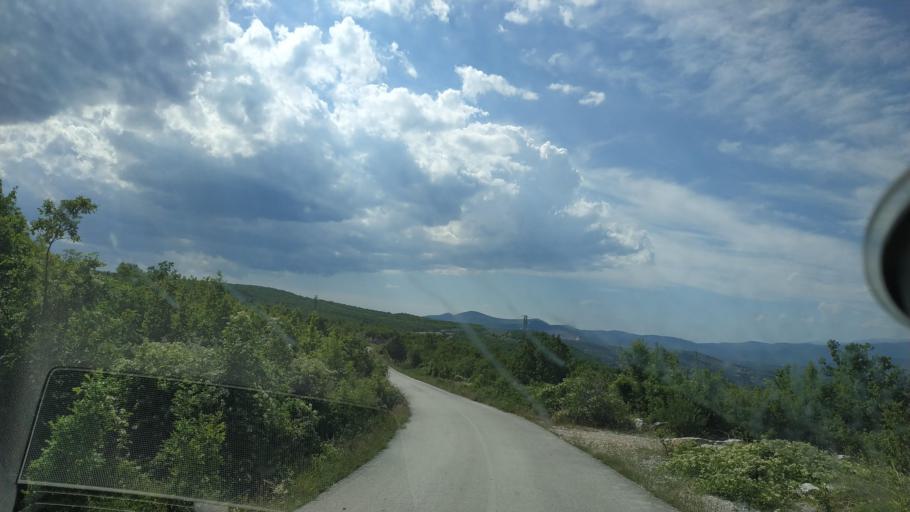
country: HR
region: Splitsko-Dalmatinska
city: Dugopolje
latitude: 43.5806
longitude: 16.6545
